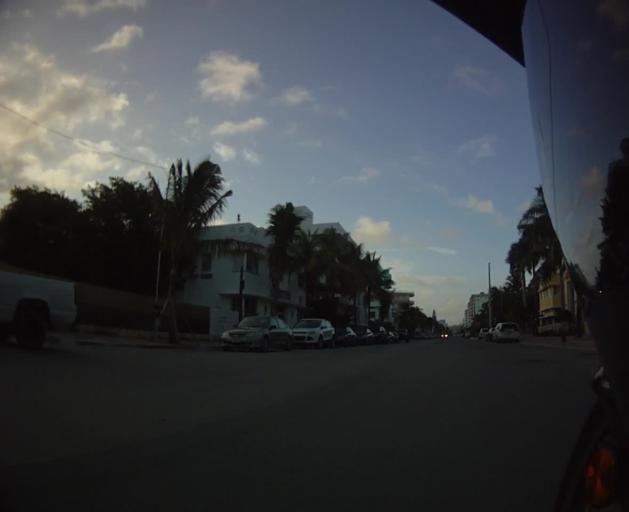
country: US
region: Florida
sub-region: Miami-Dade County
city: Miami Beach
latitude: 25.7701
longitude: -80.1329
